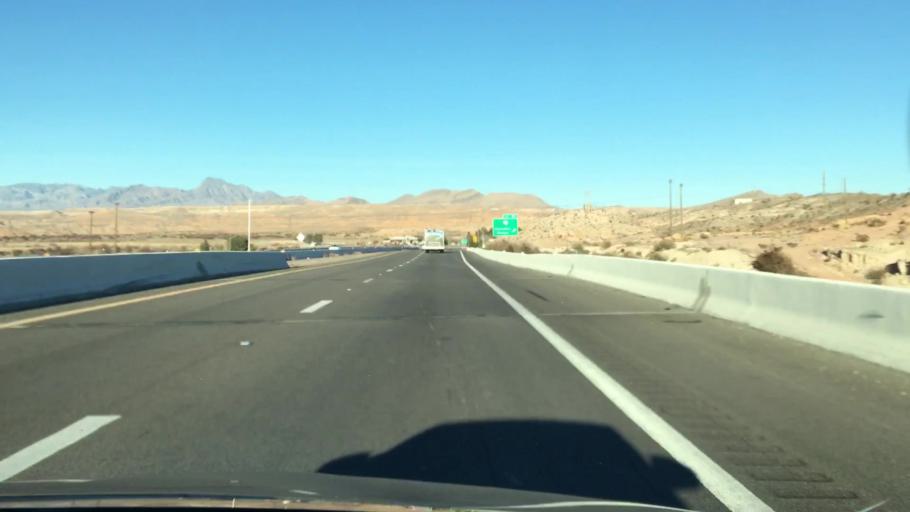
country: US
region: Nevada
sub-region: Clark County
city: Moapa Town
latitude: 36.6587
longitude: -114.5759
